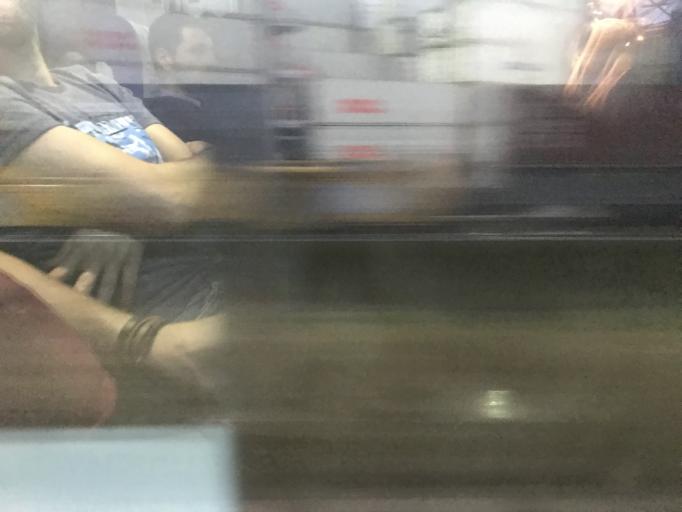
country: TR
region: Kocaeli
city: Ulasli
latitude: 40.7767
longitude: 29.7109
